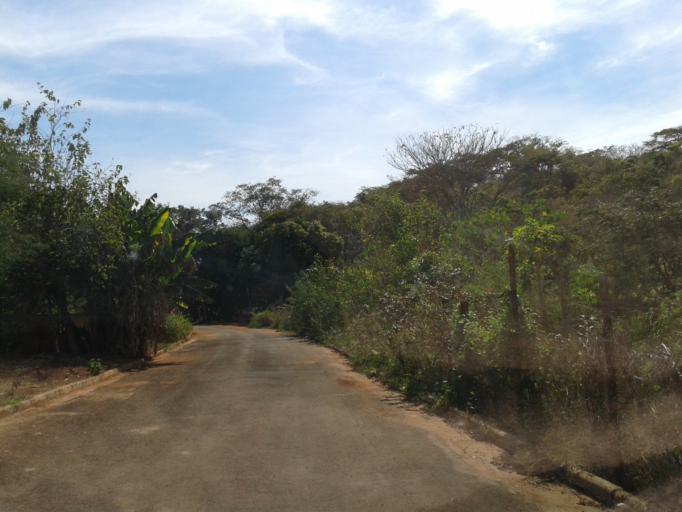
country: BR
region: Minas Gerais
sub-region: Ituiutaba
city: Ituiutaba
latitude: -18.9616
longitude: -49.4633
